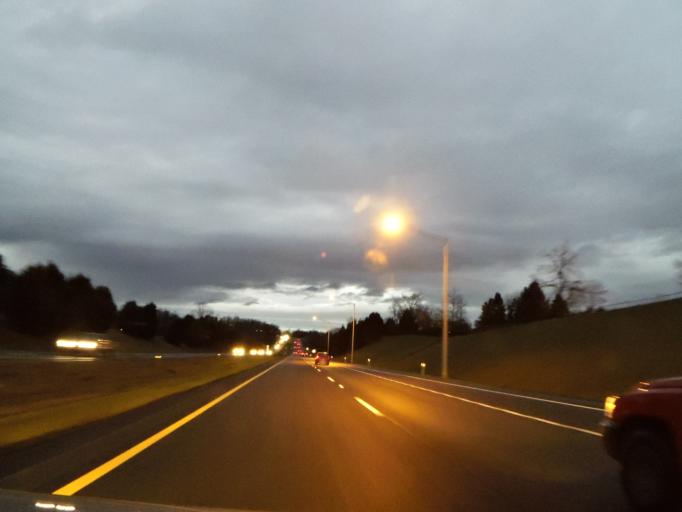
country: US
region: Tennessee
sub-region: Washington County
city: Gray
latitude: 36.4106
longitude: -82.4829
